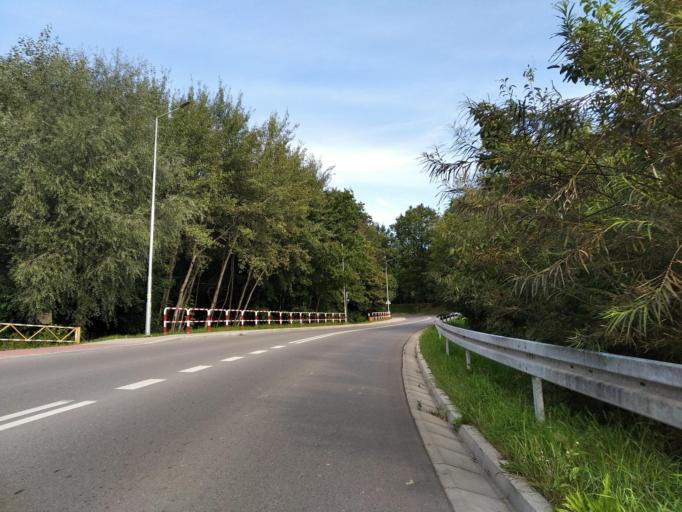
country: PL
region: Subcarpathian Voivodeship
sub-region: Powiat ropczycko-sedziszowski
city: Ropczyce
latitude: 50.0593
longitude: 21.6149
